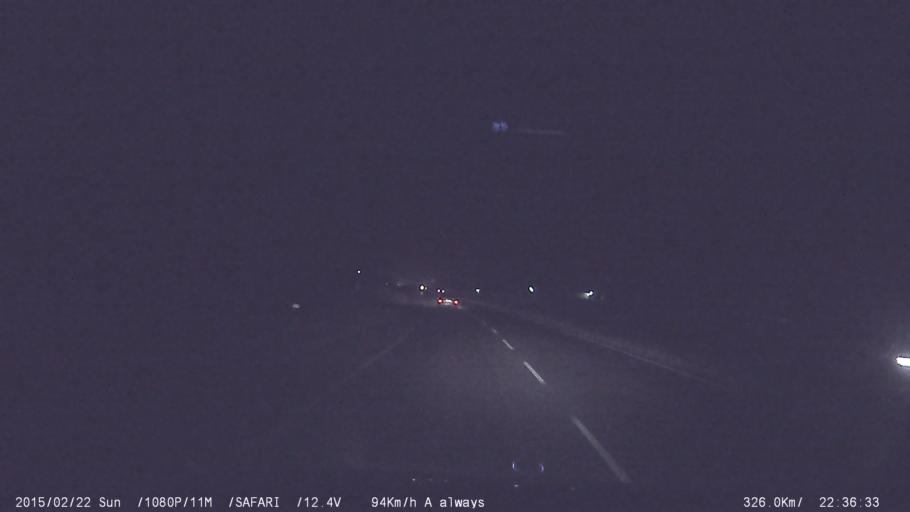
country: IN
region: Tamil Nadu
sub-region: Namakkal
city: Velur
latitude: 11.1471
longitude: 78.0243
